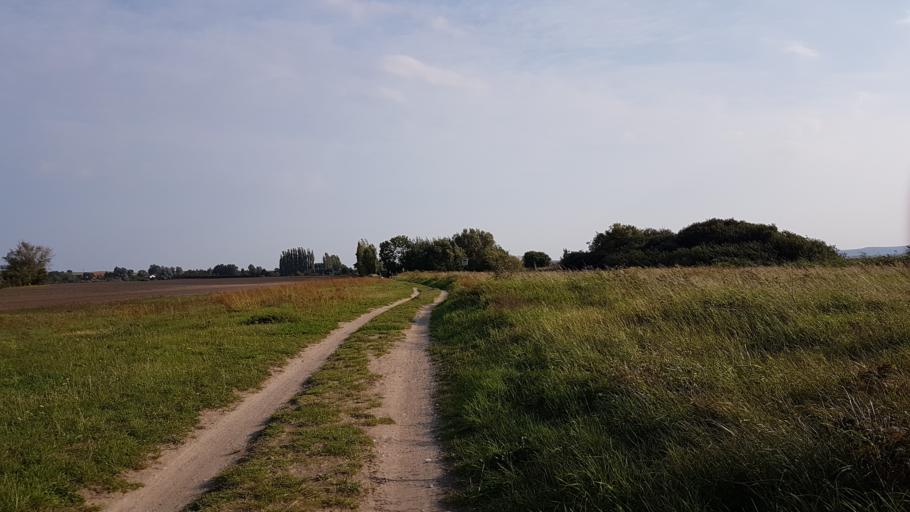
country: DE
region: Mecklenburg-Vorpommern
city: Glowe
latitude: 54.5507
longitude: 13.5019
